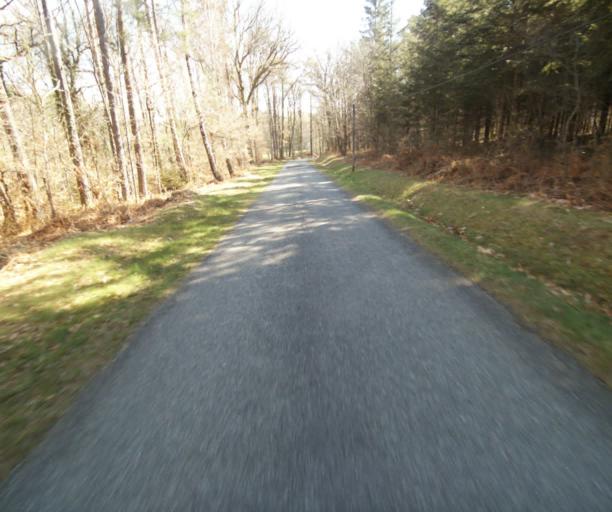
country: FR
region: Limousin
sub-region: Departement de la Correze
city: Laguenne
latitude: 45.2392
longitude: 1.9142
